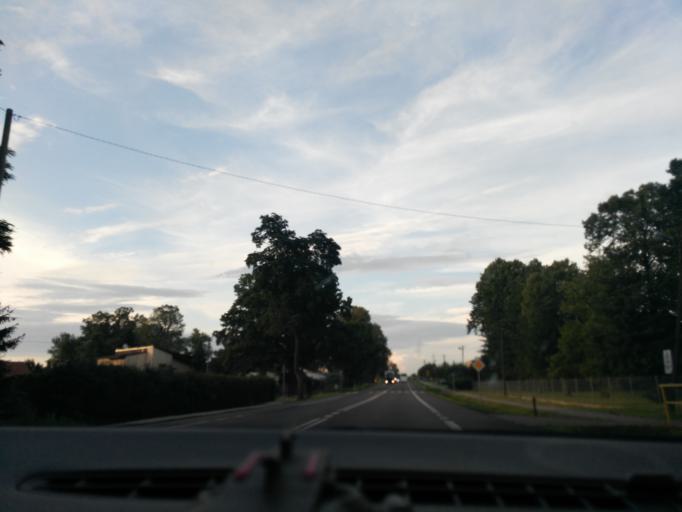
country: PL
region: Lublin Voivodeship
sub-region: Powiat lubelski
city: Niedrzwica Duza
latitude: 51.0917
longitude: 22.3652
